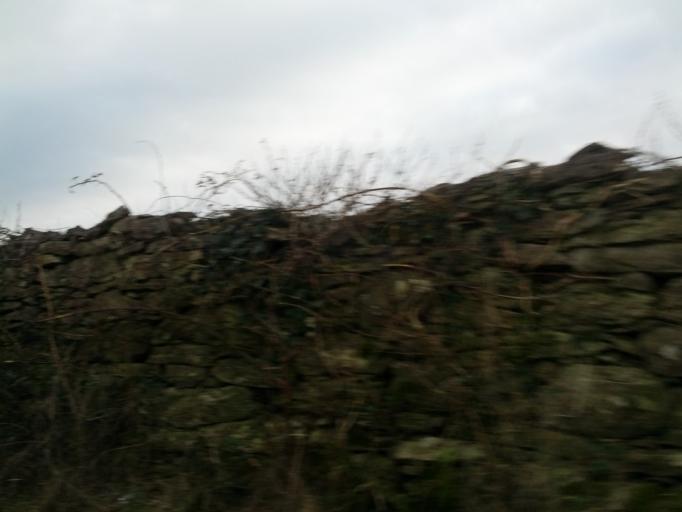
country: IE
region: Connaught
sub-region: County Galway
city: Oranmore
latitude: 53.1689
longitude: -8.8843
